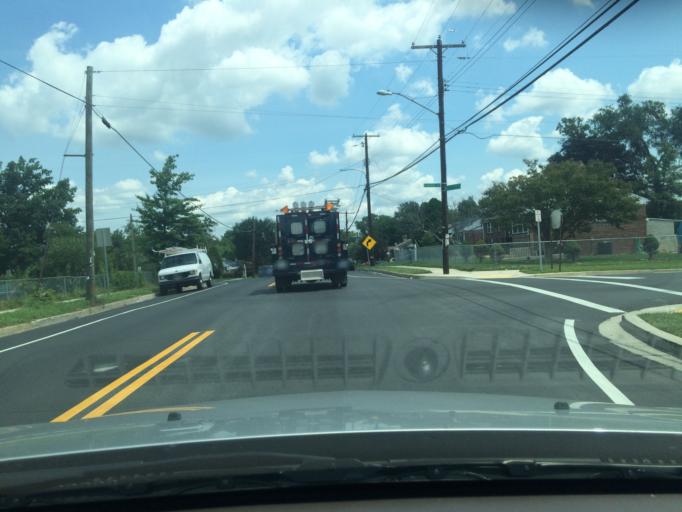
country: US
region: Maryland
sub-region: Prince George's County
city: Langley Park
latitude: 38.9881
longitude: -76.9751
